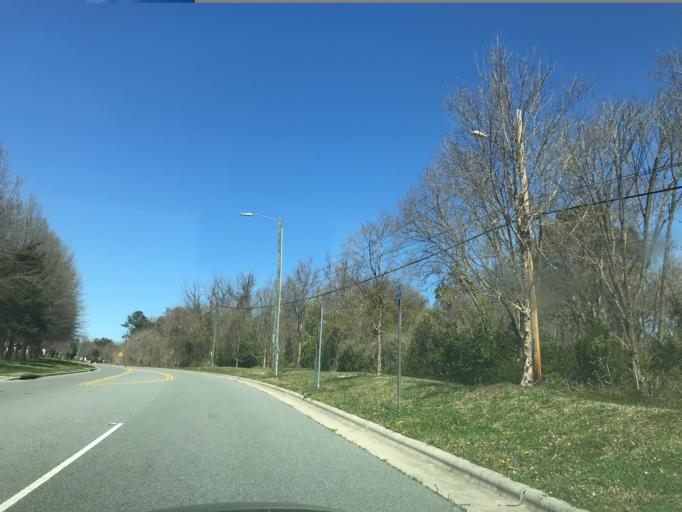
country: US
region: North Carolina
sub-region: Wake County
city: Raleigh
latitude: 35.7586
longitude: -78.6415
